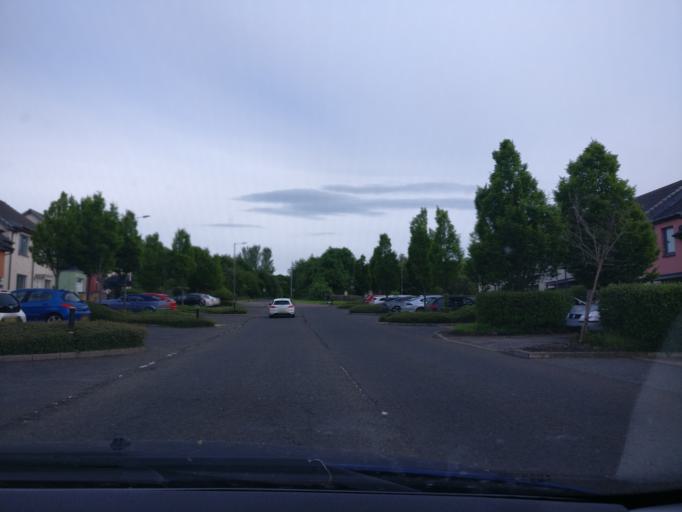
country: GB
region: Scotland
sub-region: West Lothian
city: Seafield
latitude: 55.9308
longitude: -3.1401
